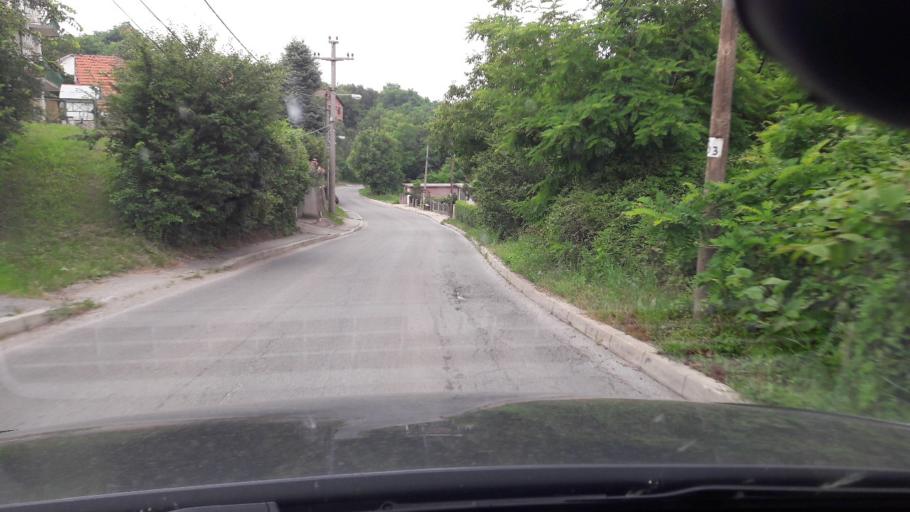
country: RS
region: Central Serbia
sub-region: Belgrade
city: Grocka
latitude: 44.6574
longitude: 20.5928
